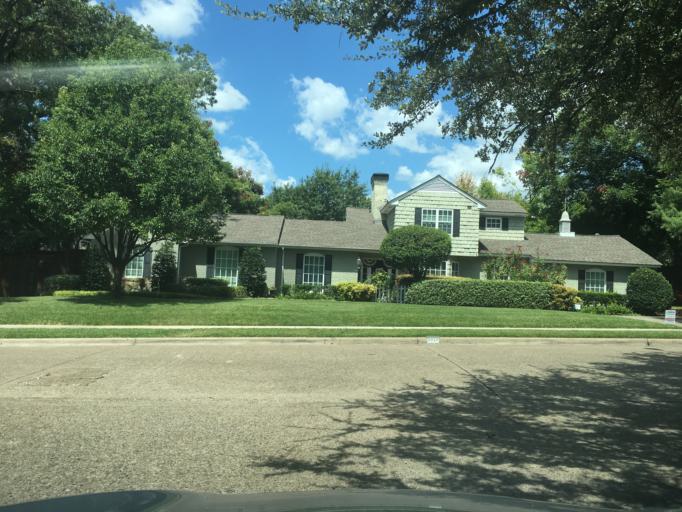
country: US
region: Texas
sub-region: Dallas County
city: Richardson
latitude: 32.8705
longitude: -96.7121
